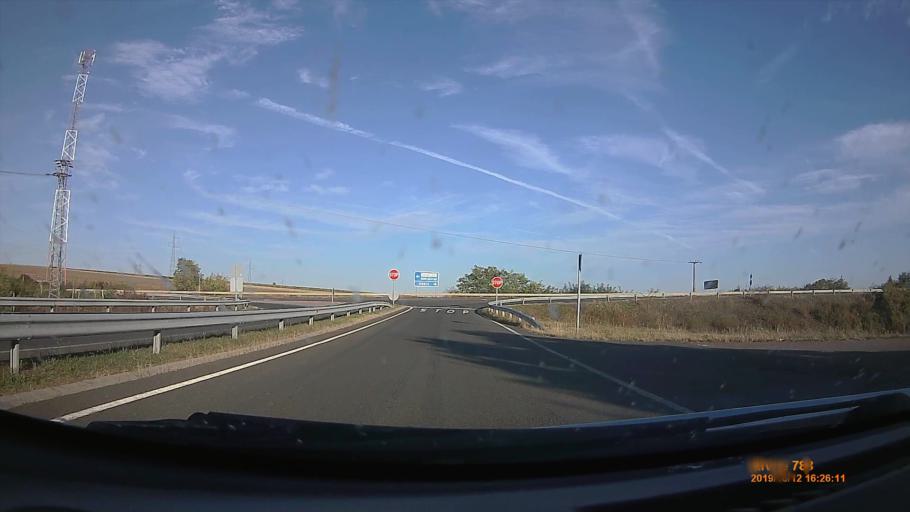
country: HU
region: Heves
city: Gyongyoshalasz
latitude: 47.7337
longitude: 19.9582
